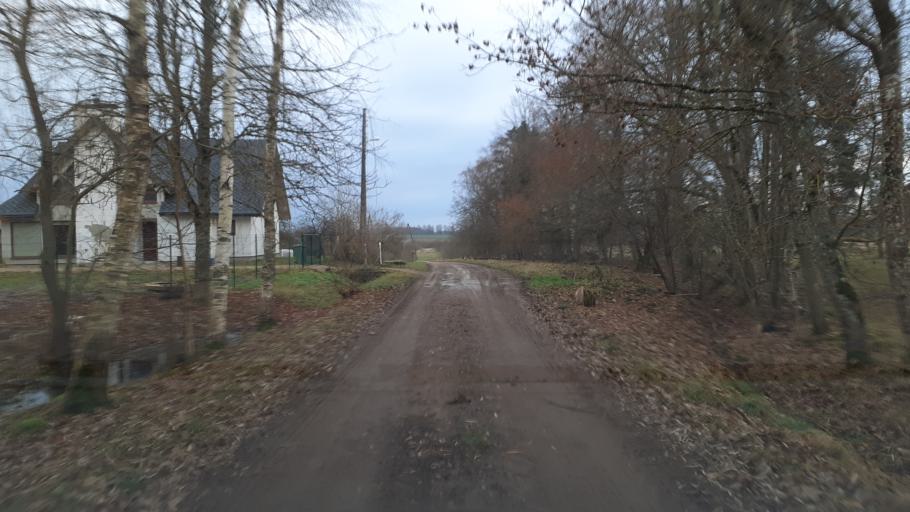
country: LV
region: Aizpute
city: Aizpute
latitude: 56.8012
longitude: 21.6681
